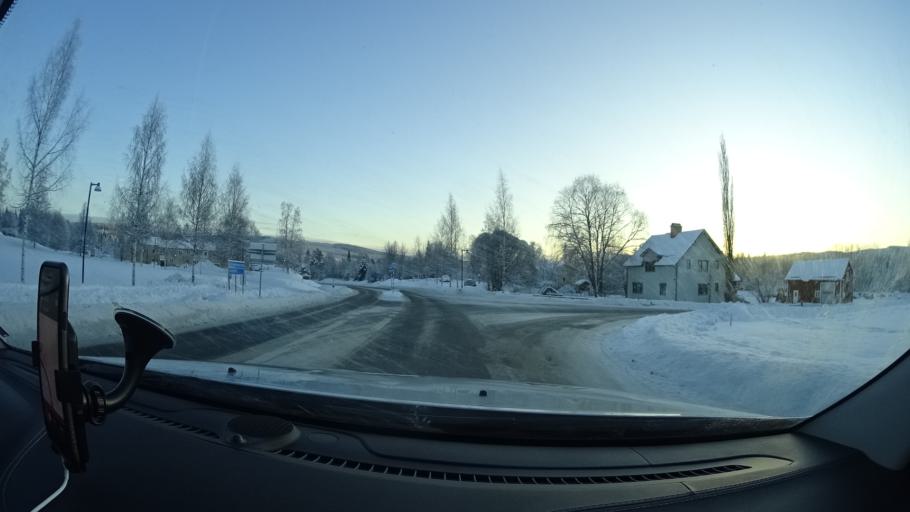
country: SE
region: Jaemtland
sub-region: Ragunda Kommun
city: Hammarstrand
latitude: 63.0132
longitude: 16.6550
